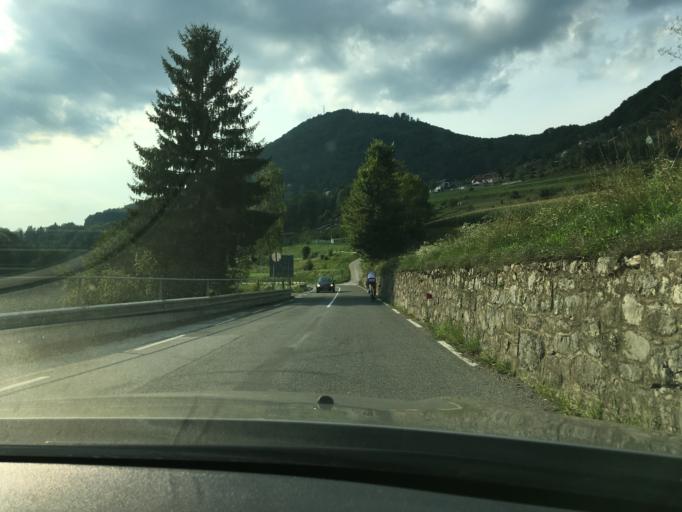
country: SI
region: Dolenjske Toplice
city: Dolenjske Toplice
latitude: 45.7800
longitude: 15.0184
